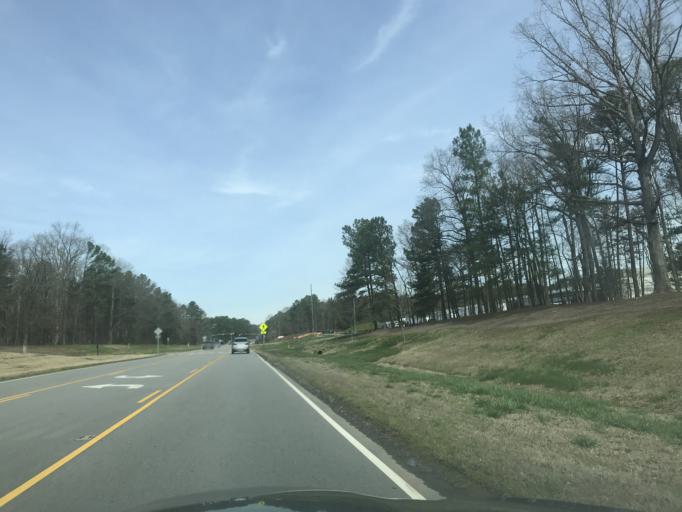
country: US
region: North Carolina
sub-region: Wake County
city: Morrisville
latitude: 35.8954
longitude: -78.8795
